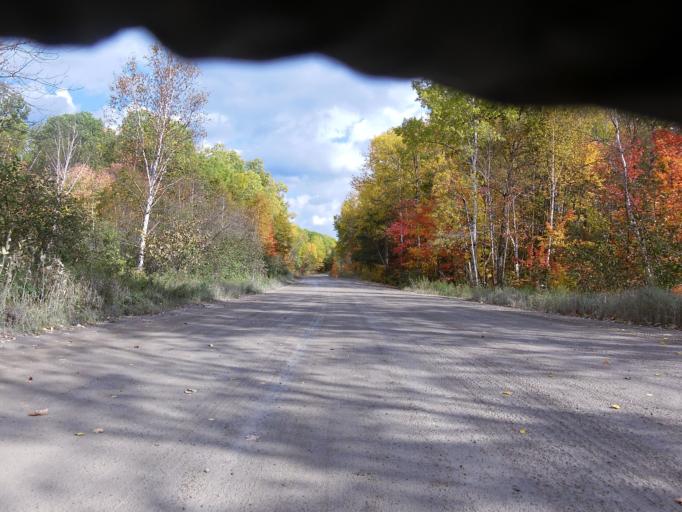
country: CA
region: Ontario
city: Petawawa
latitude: 45.8093
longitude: -77.3559
